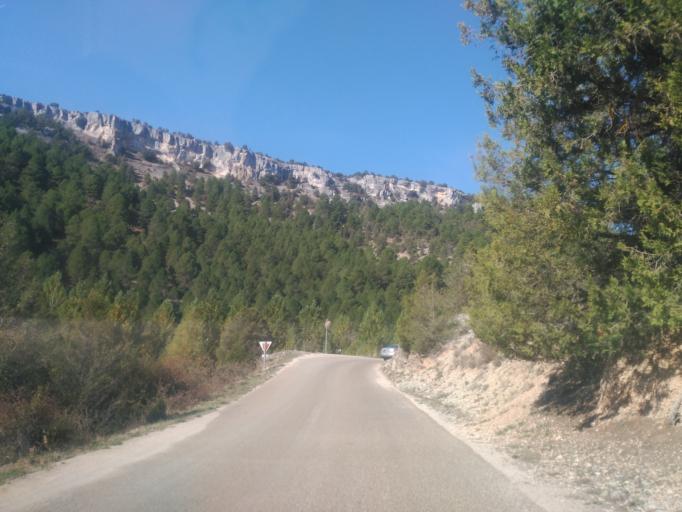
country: ES
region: Castille and Leon
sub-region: Provincia de Soria
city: Ucero
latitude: 41.7334
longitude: -3.0469
